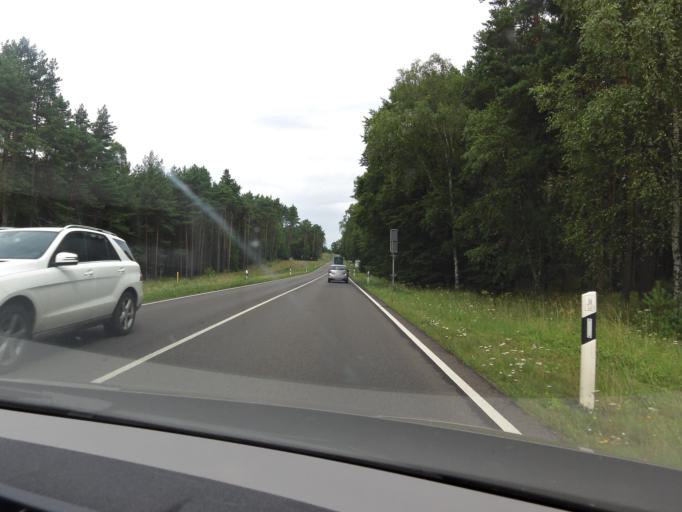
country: DE
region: Mecklenburg-Vorpommern
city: Neustrelitz
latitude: 53.2953
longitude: 13.1071
